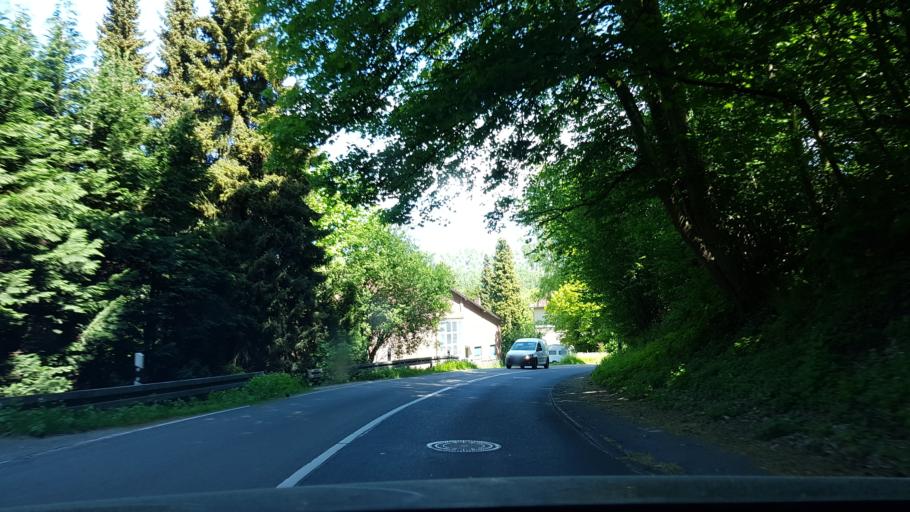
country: DE
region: North Rhine-Westphalia
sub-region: Regierungsbezirk Dusseldorf
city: Heiligenhaus
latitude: 51.3055
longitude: 6.9461
